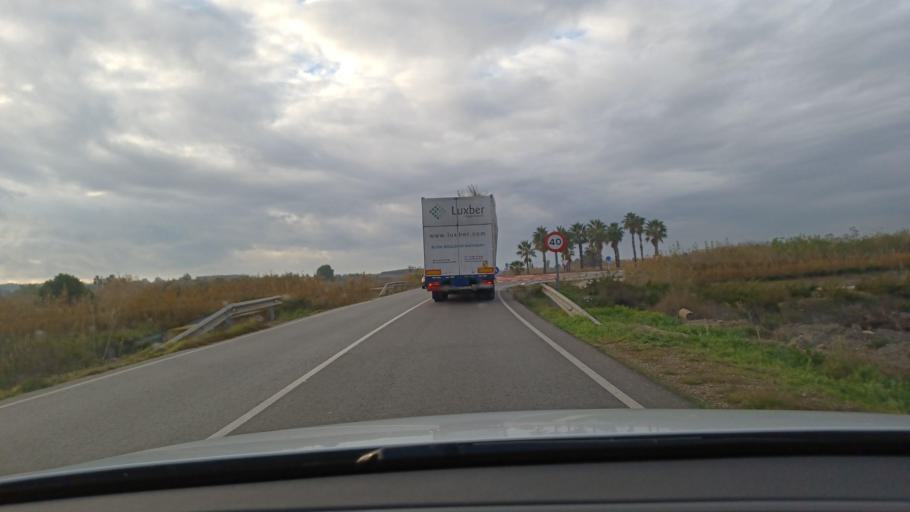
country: ES
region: Valencia
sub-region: Provincia de Alicante
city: Daya Vieja
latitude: 38.1602
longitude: -0.7030
